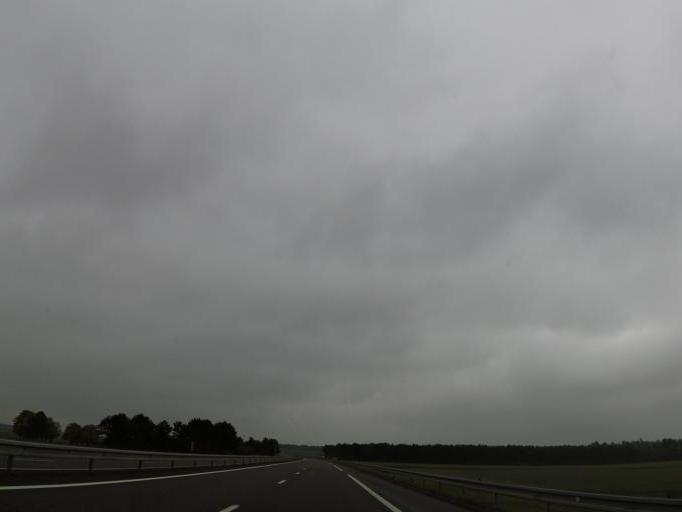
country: FR
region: Champagne-Ardenne
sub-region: Departement de la Marne
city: Courtisols
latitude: 49.0279
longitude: 4.4988
